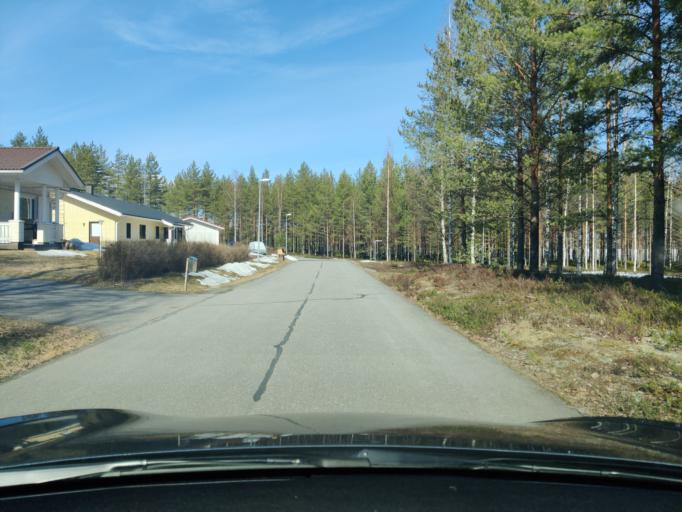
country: FI
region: Northern Savo
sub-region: Kuopio
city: Vehmersalmi
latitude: 62.7727
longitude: 27.9854
